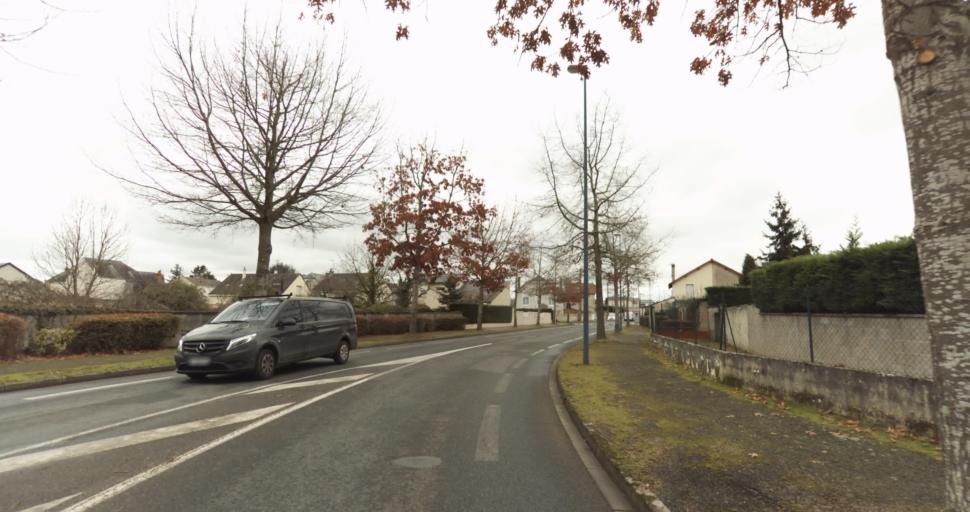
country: FR
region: Pays de la Loire
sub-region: Departement de Maine-et-Loire
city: Saumur
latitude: 47.2518
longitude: -0.0938
